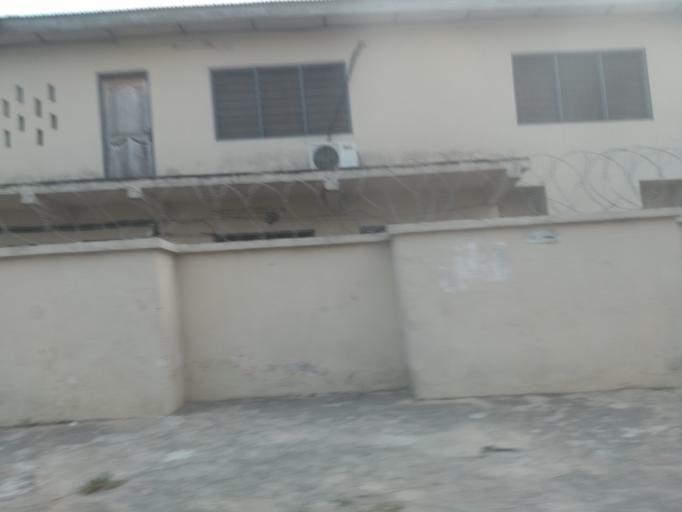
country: GH
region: Ashanti
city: Tafo
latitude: 6.7095
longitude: -1.6105
